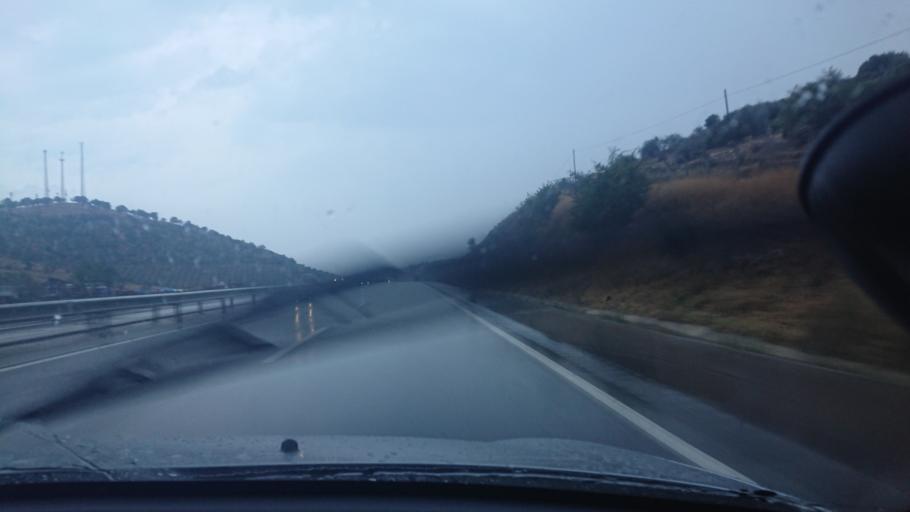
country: TR
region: Manisa
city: Menye
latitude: 38.5439
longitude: 28.4487
